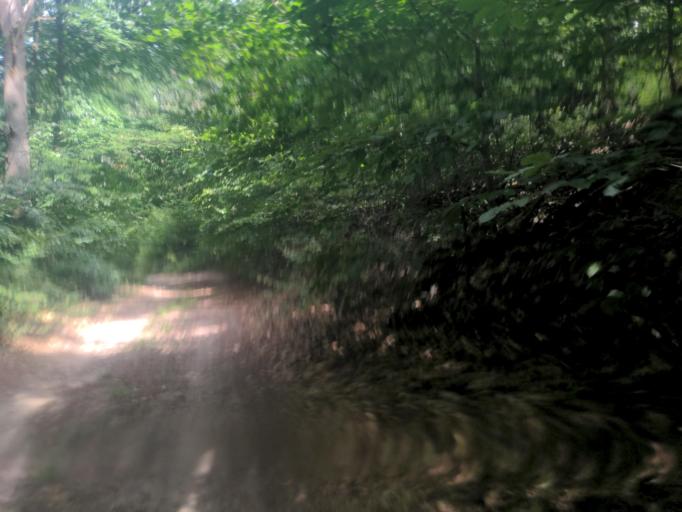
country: DE
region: Lower Saxony
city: Neu Darchau
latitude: 53.2227
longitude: 10.8586
